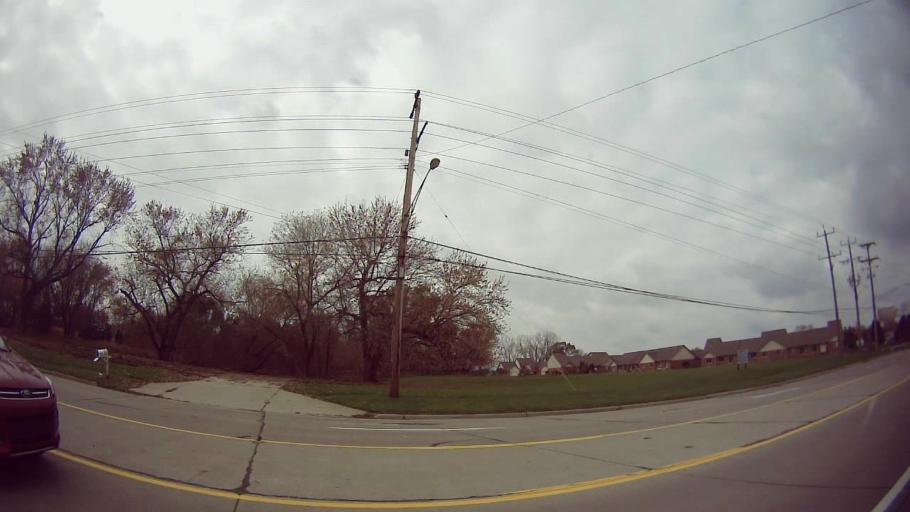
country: US
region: Michigan
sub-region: Oakland County
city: Madison Heights
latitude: 42.5286
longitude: -83.0682
